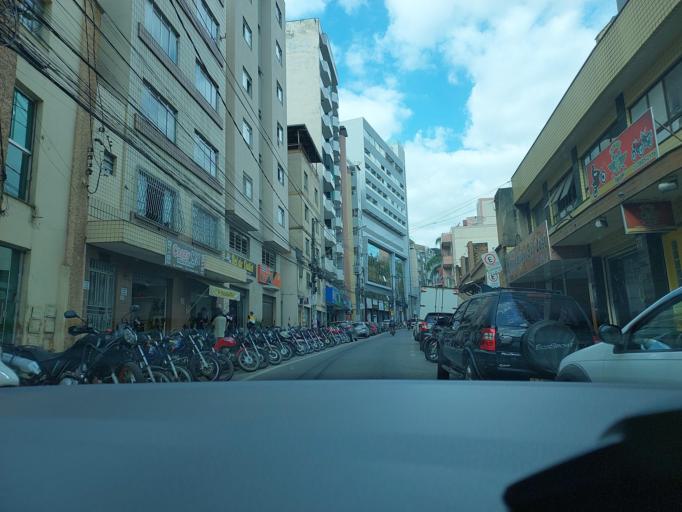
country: BR
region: Minas Gerais
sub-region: Vicosa
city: Vicosa
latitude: -20.7519
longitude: -42.8818
